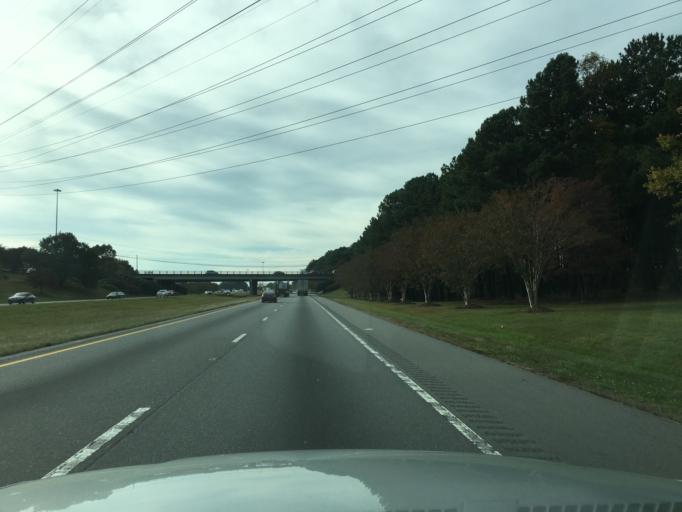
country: US
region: North Carolina
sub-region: Catawba County
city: Hickory
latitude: 35.7130
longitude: -81.3102
